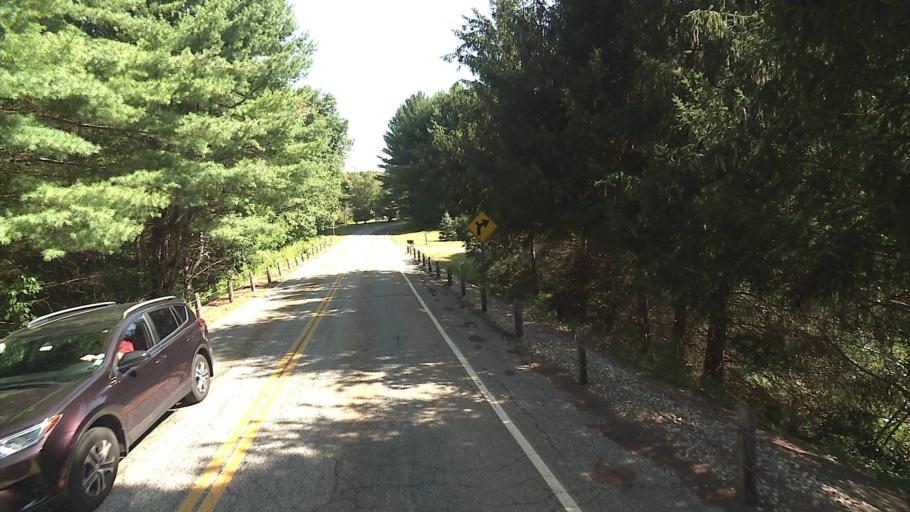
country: US
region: Connecticut
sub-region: Litchfield County
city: Thomaston
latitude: 41.7087
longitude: -73.0617
